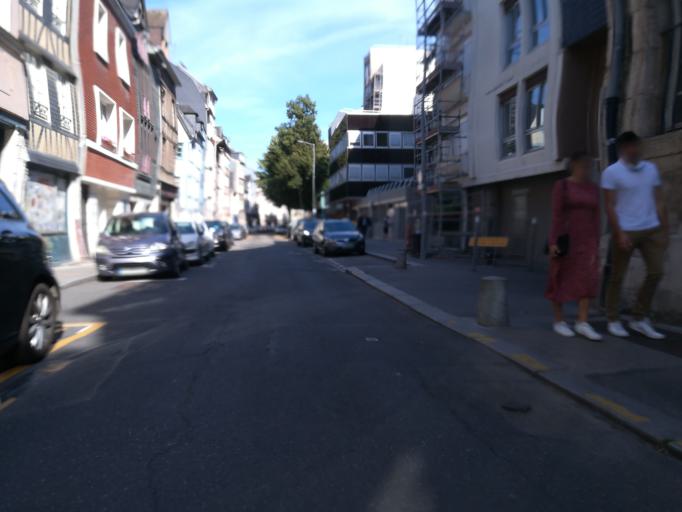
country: FR
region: Haute-Normandie
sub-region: Departement de la Seine-Maritime
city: Rouen
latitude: 49.4437
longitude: 1.1020
